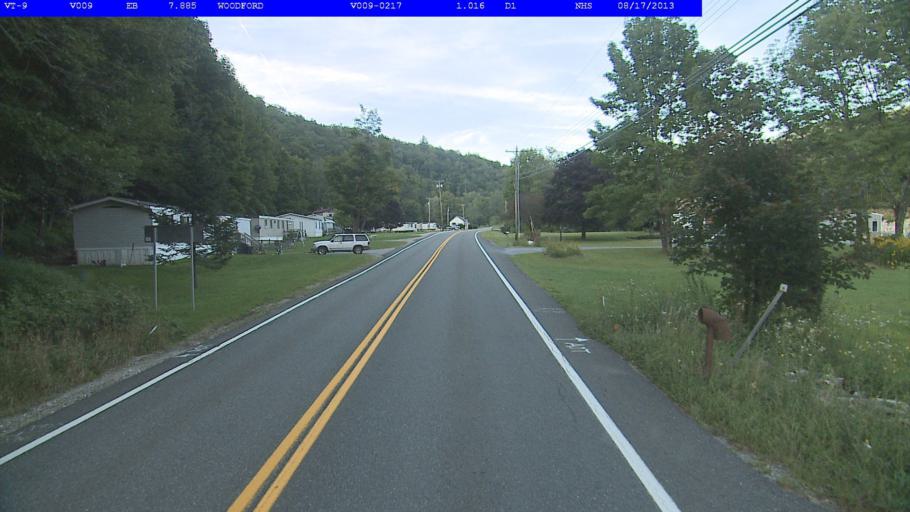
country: US
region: Vermont
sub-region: Bennington County
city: Bennington
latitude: 42.8939
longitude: -73.1365
